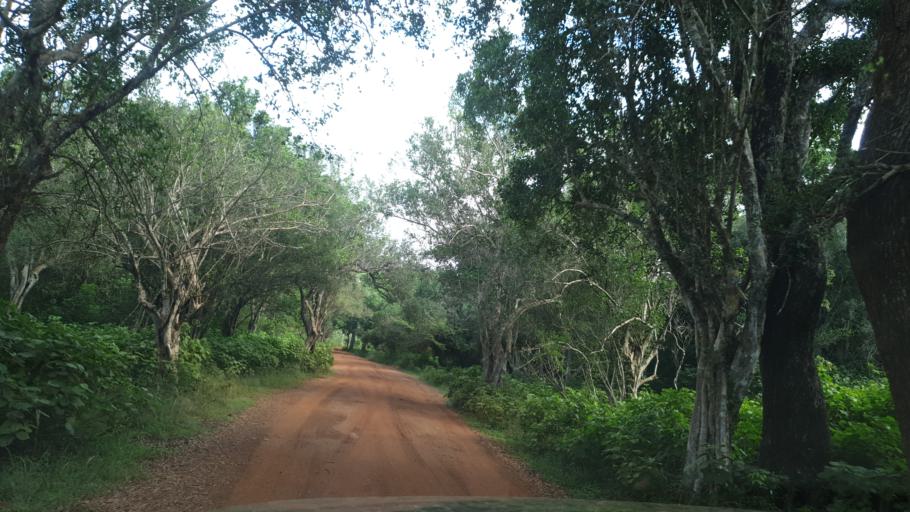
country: LK
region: North Central
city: Anuradhapura
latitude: 8.3791
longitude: 80.0681
